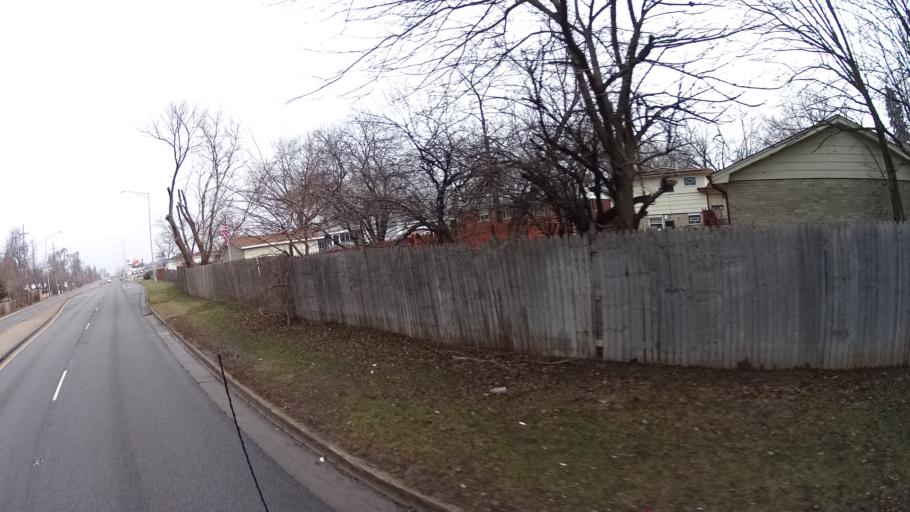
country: US
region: Illinois
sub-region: Cook County
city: East Hazel Crest
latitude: 41.5517
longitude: -87.6359
